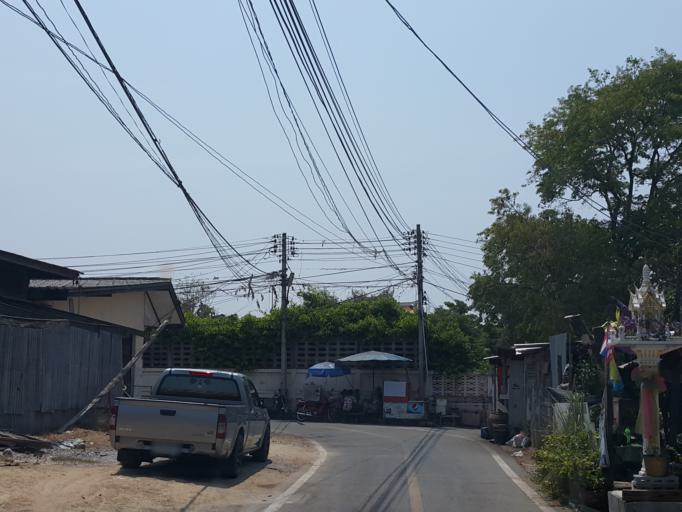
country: TH
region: Kanchanaburi
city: Kanchanaburi
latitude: 14.0288
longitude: 99.5241
